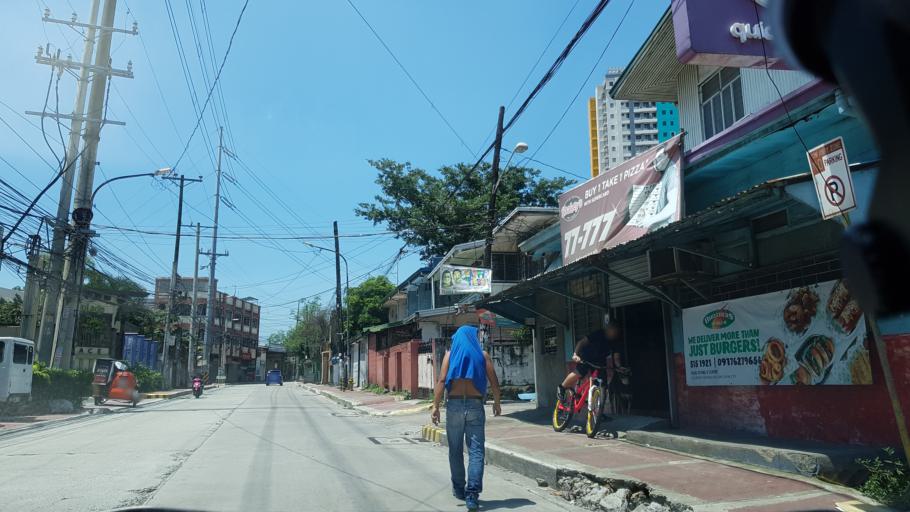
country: PH
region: Metro Manila
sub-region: San Juan
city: San Juan
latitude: 14.6155
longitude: 121.0458
